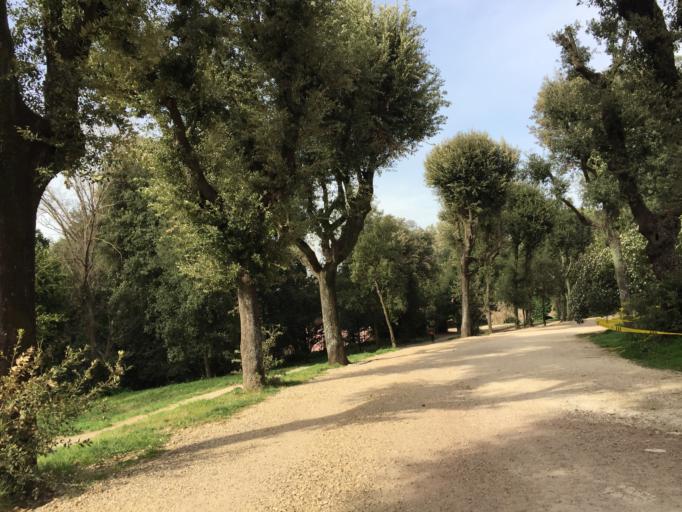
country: VA
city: Vatican City
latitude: 41.8875
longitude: 12.4541
